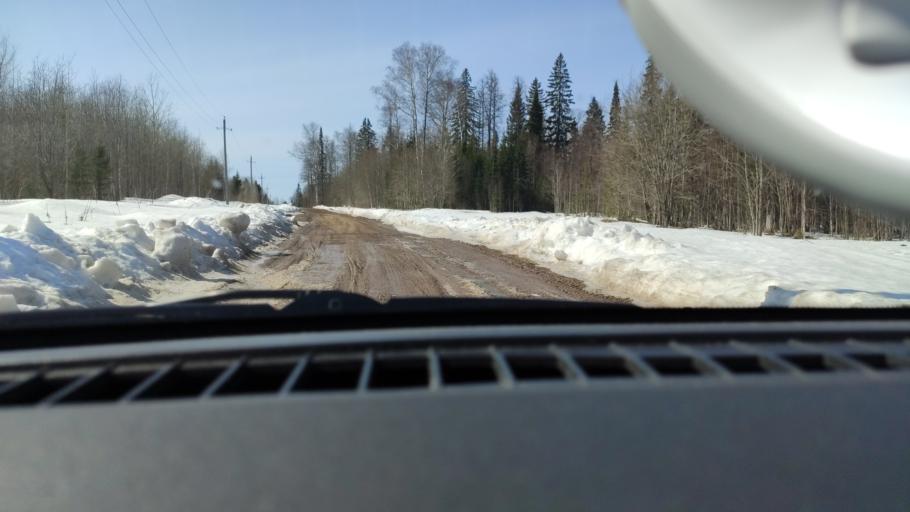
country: RU
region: Perm
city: Perm
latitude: 58.2202
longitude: 56.1596
